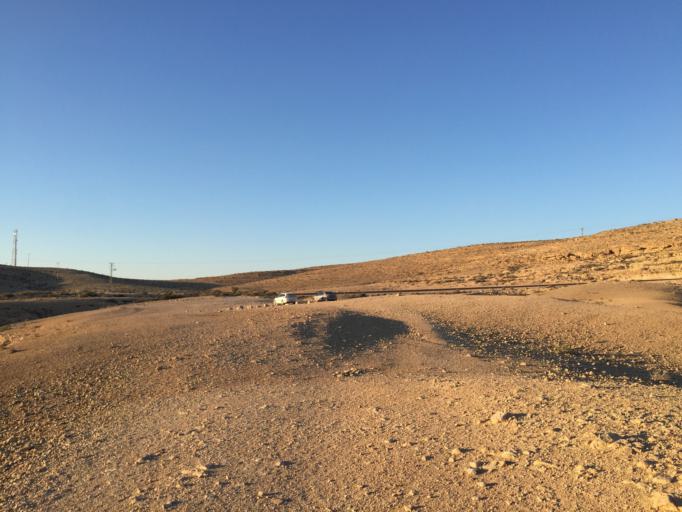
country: IL
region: Southern District
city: Midreshet Ben-Gurion
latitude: 30.8466
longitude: 34.7550
